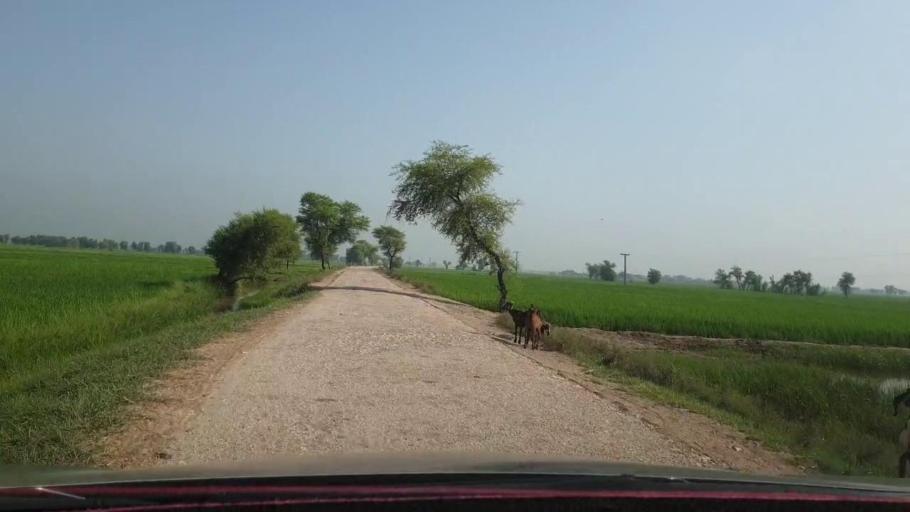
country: PK
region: Sindh
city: Nasirabad
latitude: 27.4868
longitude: 67.9262
